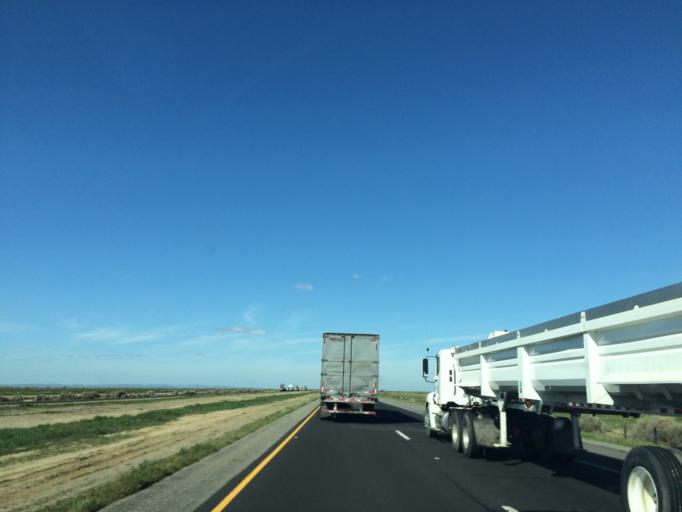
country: US
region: California
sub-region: Kern County
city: Lost Hills
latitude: 35.7666
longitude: -119.7650
